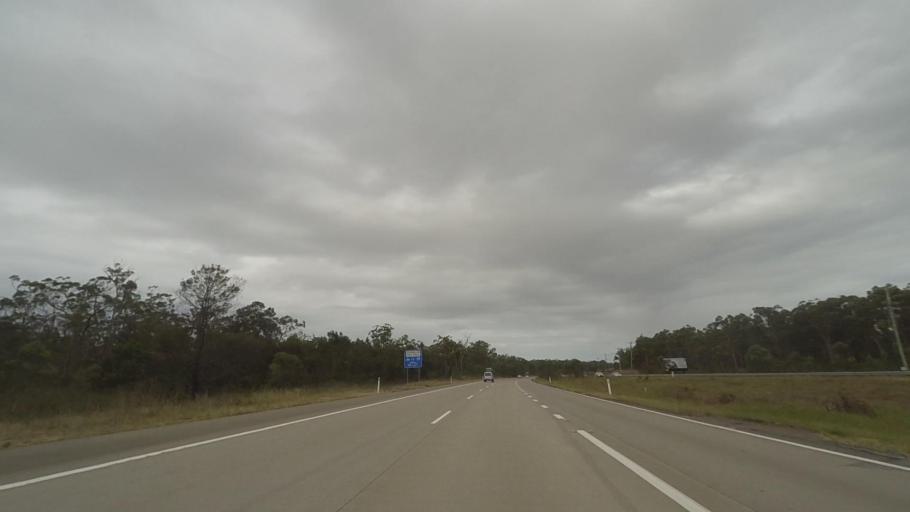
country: AU
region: New South Wales
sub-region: Port Stephens Shire
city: Port Stephens
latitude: -32.6131
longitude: 152.0803
